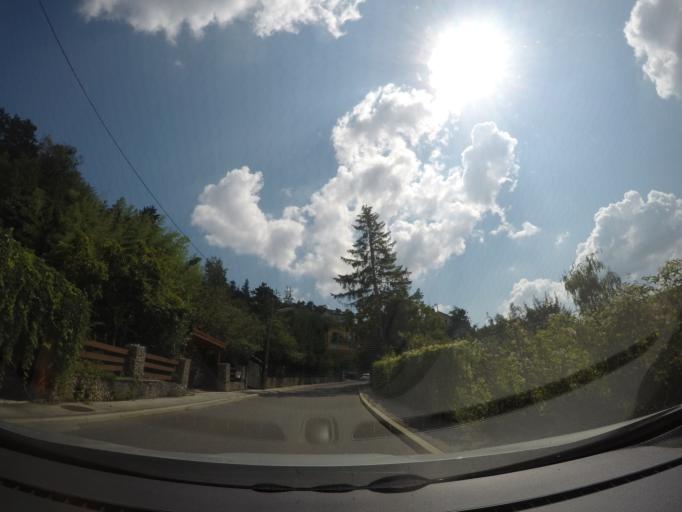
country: AT
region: Lower Austria
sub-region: Politischer Bezirk Wien-Umgebung
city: Purkersdorf
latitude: 48.2182
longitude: 16.2546
